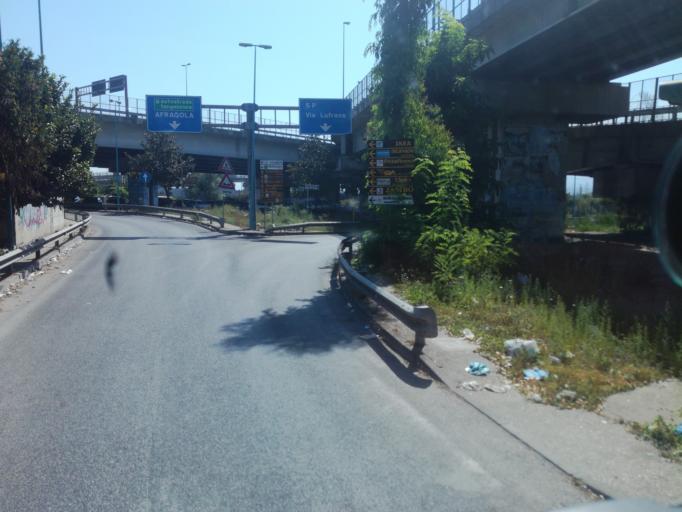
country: IT
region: Campania
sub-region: Provincia di Napoli
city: Arpino
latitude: 40.8920
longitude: 14.3249
